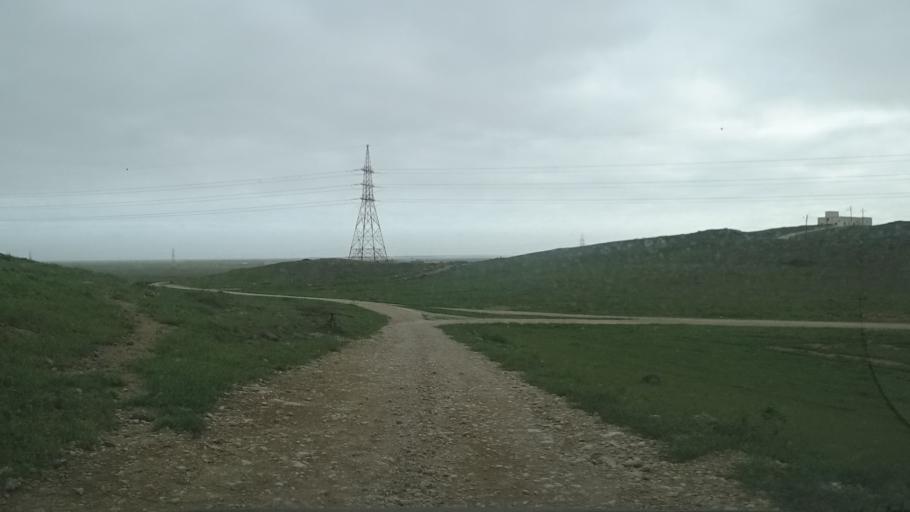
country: OM
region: Zufar
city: Salalah
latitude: 17.1122
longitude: 54.2369
